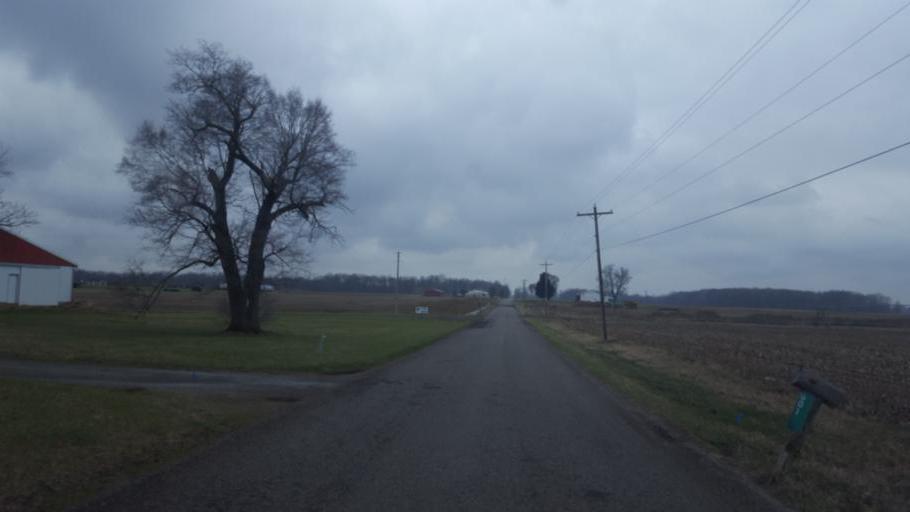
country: US
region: Ohio
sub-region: Delaware County
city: Ashley
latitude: 40.3766
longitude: -82.8538
